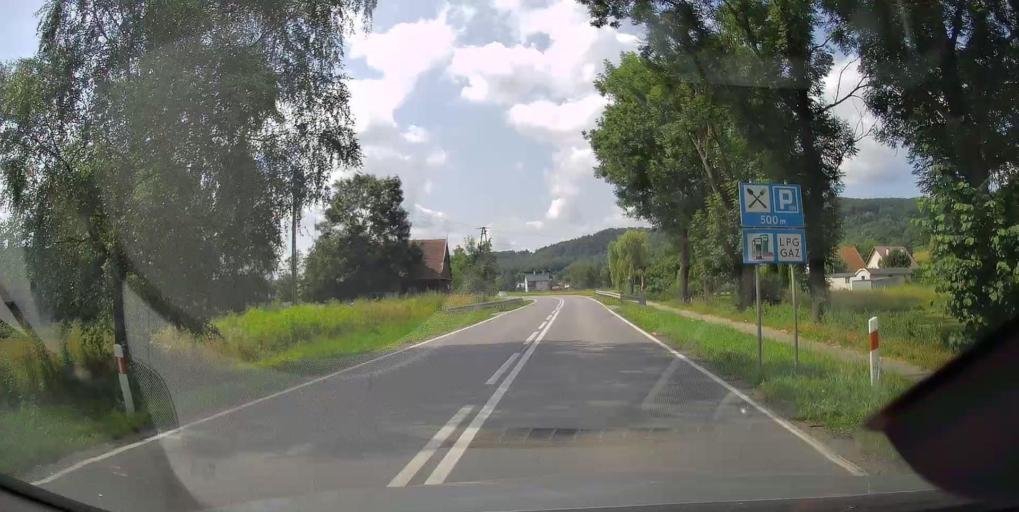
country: PL
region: Lesser Poland Voivodeship
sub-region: Powiat tarnowski
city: Wielka Wies
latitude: 49.9045
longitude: 20.8165
